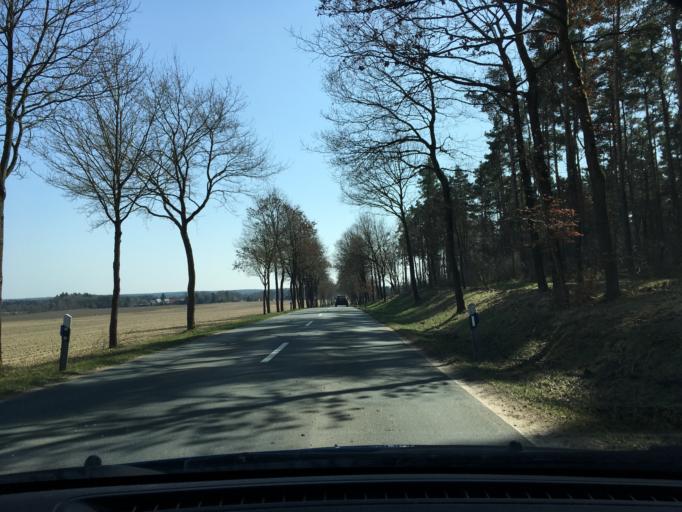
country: DE
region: Lower Saxony
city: Eimke
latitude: 52.9833
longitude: 10.3080
